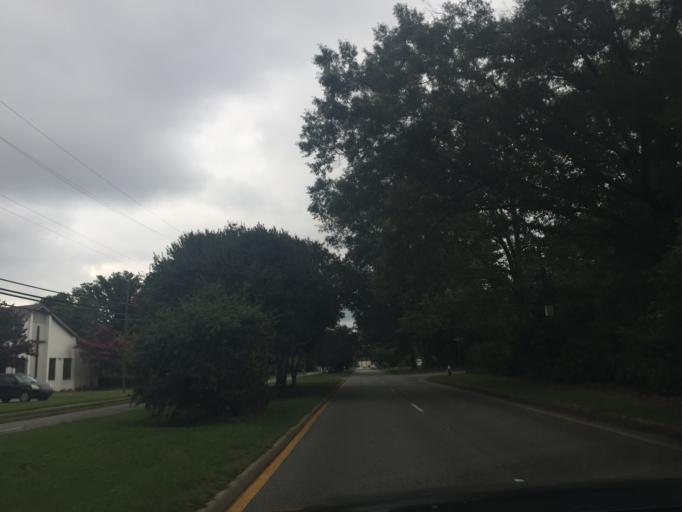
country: US
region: Virginia
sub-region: City of Newport News
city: Newport News
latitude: 37.0683
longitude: -76.4978
